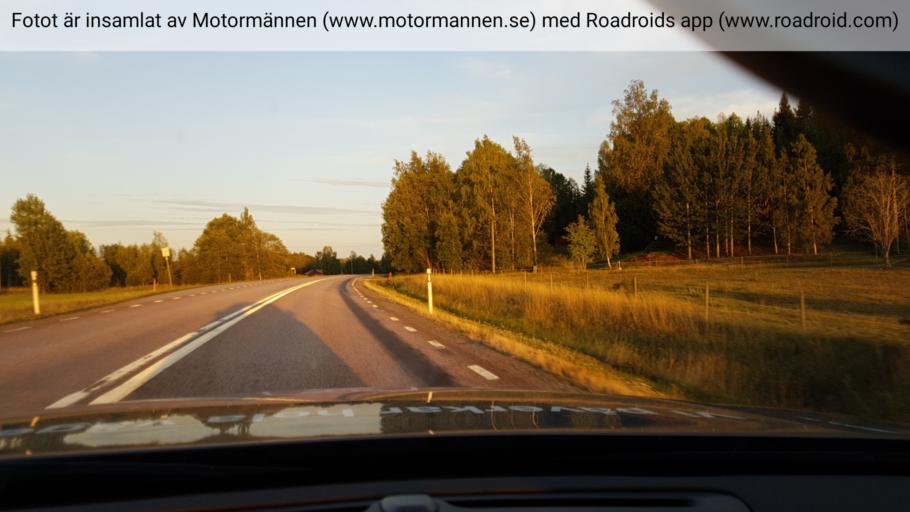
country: SE
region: OErebro
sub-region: Karlskoga Kommun
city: Karlskoga
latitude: 59.3911
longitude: 14.4668
